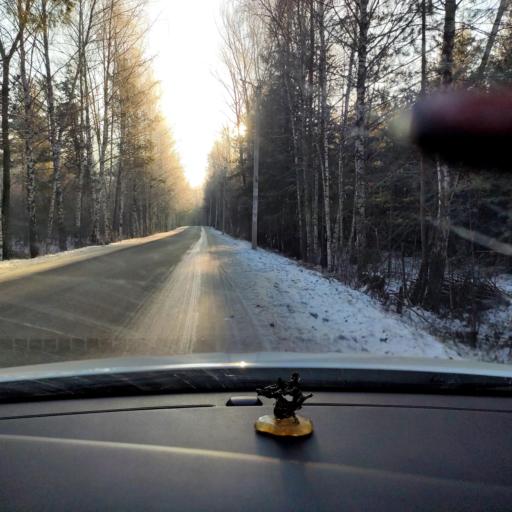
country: RU
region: Tatarstan
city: Stolbishchi
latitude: 55.6736
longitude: 49.1193
